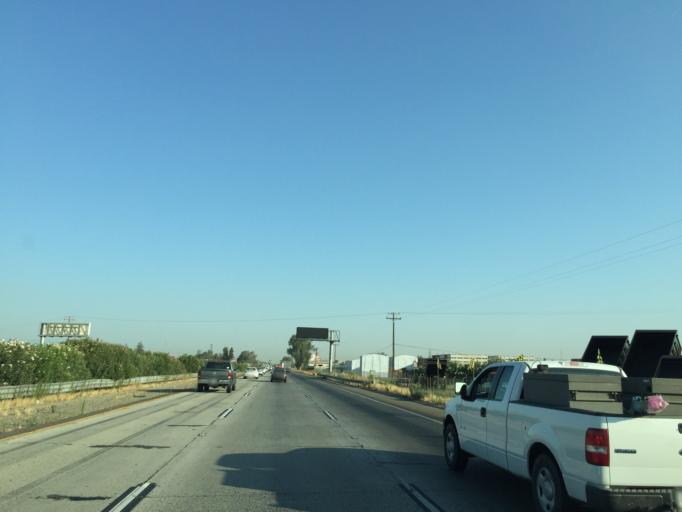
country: US
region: California
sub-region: Fresno County
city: Fowler
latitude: 36.6193
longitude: -119.6762
